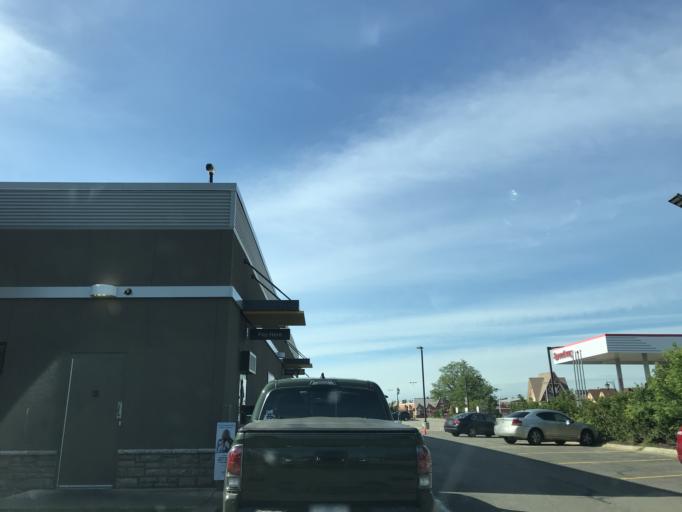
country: US
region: Michigan
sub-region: Otsego County
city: Gaylord
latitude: 45.0279
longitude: -84.6832
